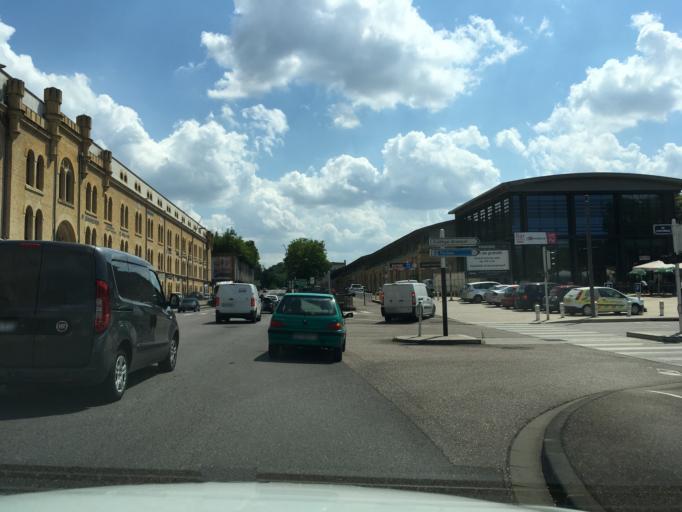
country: FR
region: Lorraine
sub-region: Departement de la Moselle
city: Metz
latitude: 49.1232
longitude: 6.1878
